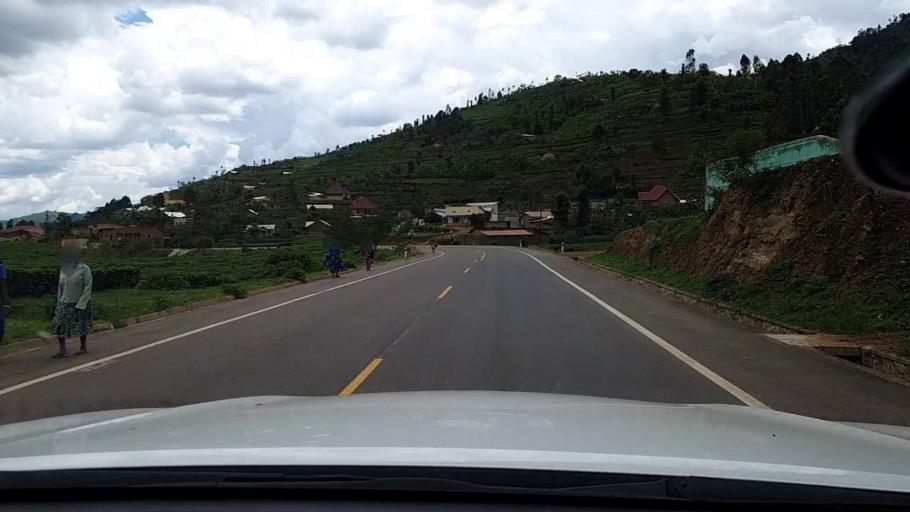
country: RW
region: Northern Province
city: Byumba
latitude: -1.6523
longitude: 29.9033
